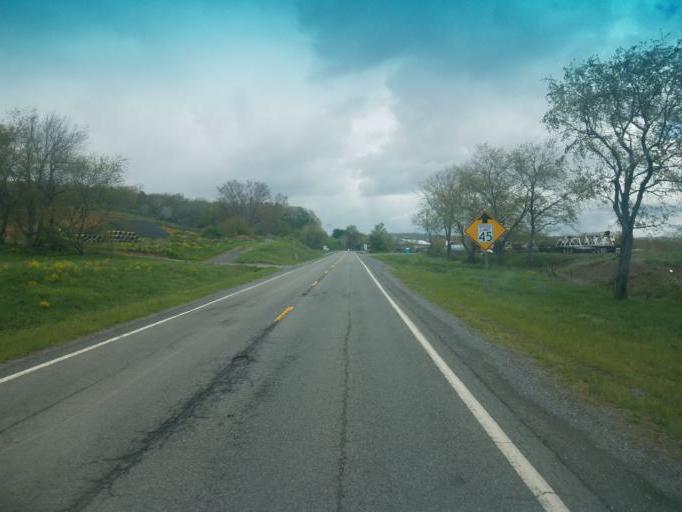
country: US
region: Virginia
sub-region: Bland County
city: Bland
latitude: 37.0970
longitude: -81.1341
